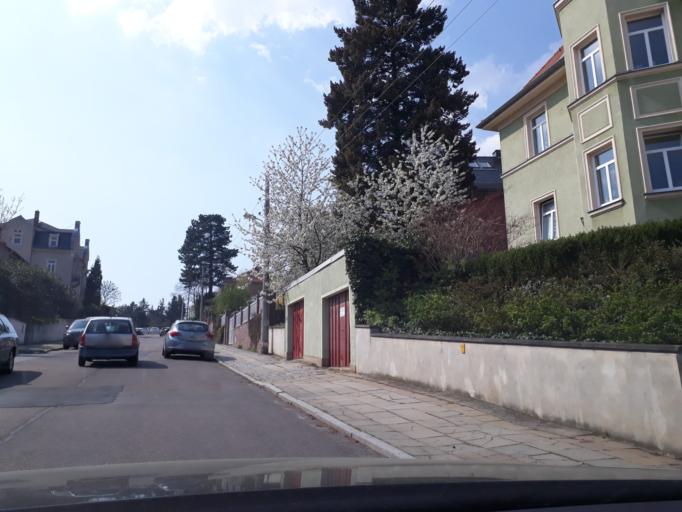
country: DE
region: Saxony
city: Dresden
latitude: 51.0110
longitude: 13.7585
